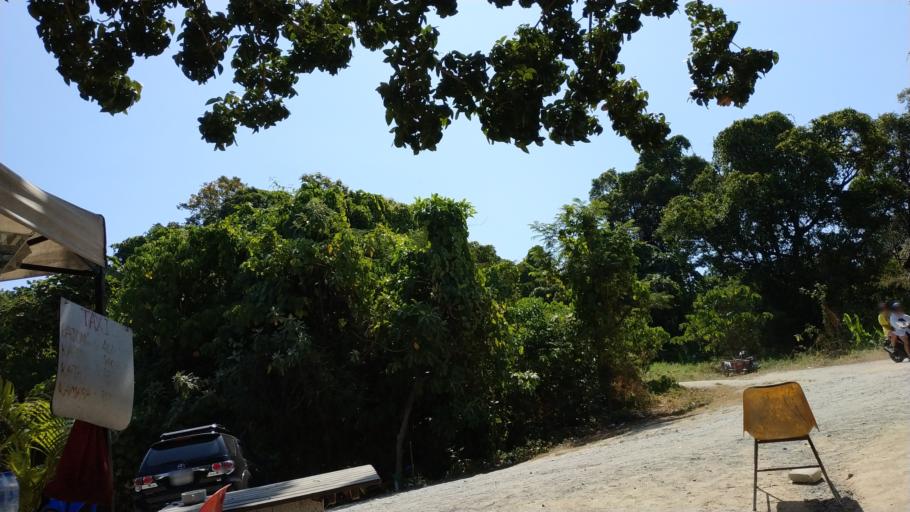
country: TH
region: Phuket
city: Patong
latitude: 7.8739
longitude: 98.2785
